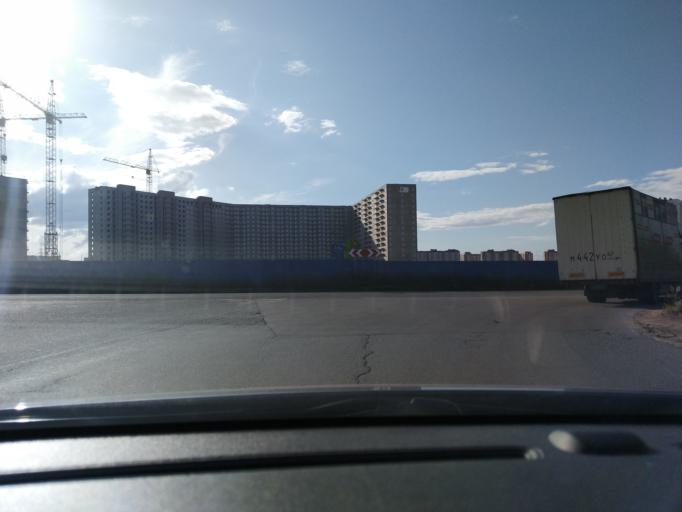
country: RU
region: St.-Petersburg
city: Gorelovo
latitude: 59.7856
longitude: 30.1667
